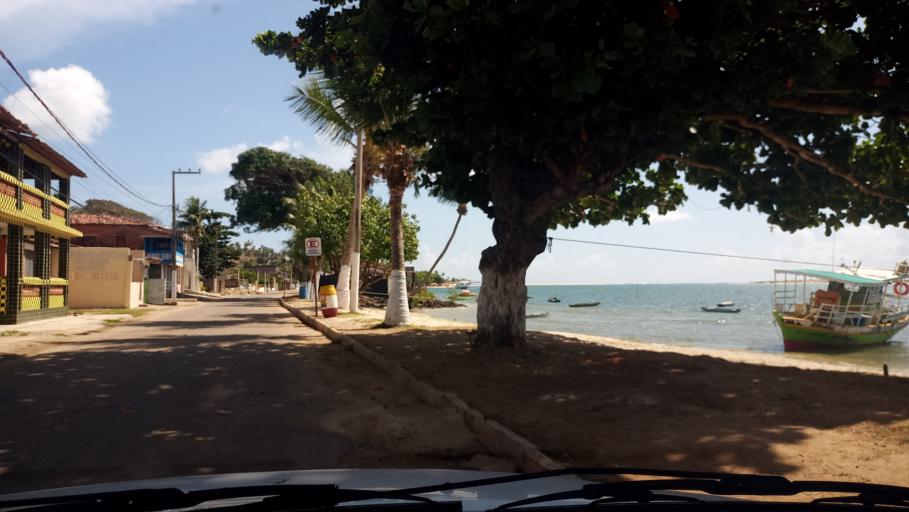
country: BR
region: Rio Grande do Norte
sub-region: Canguaretama
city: Canguaretama
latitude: -6.3187
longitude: -35.0464
